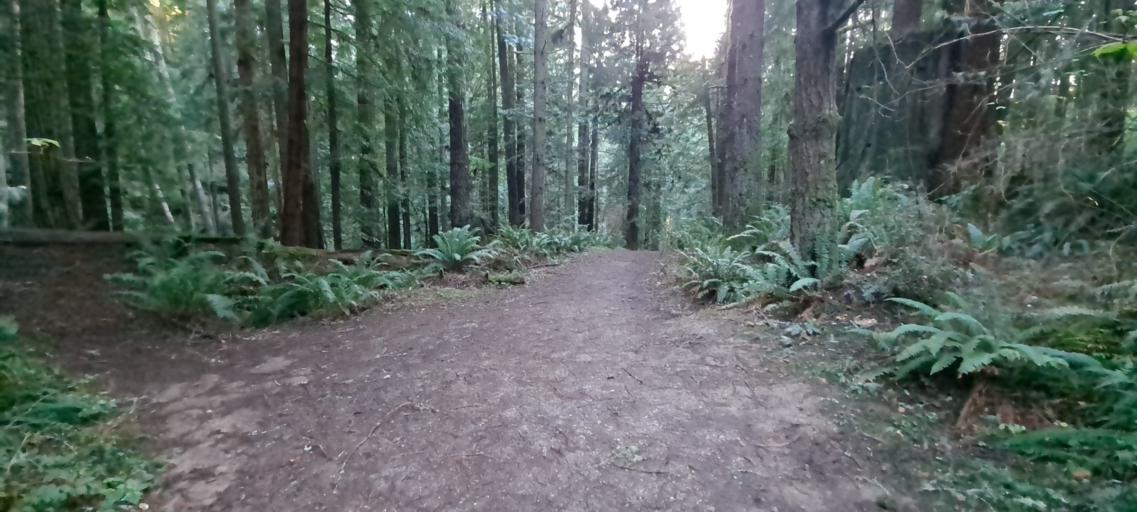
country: US
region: California
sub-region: Humboldt County
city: Arcata
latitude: 40.8718
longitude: -124.0713
